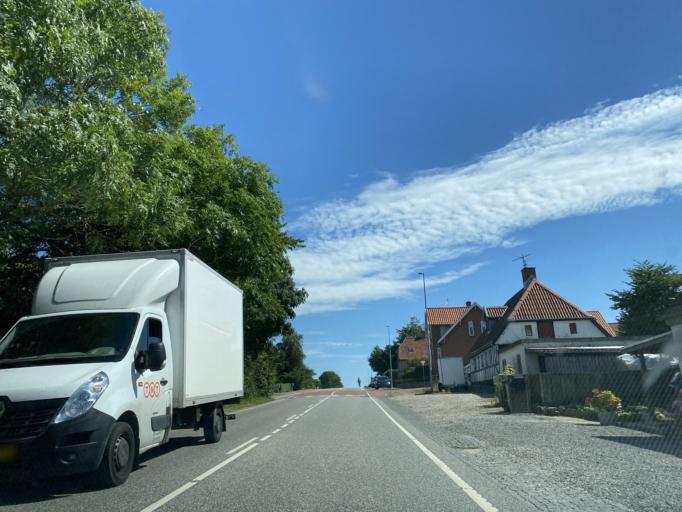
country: DK
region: South Denmark
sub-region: Faaborg-Midtfyn Kommune
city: Faaborg
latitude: 55.1094
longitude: 10.1612
